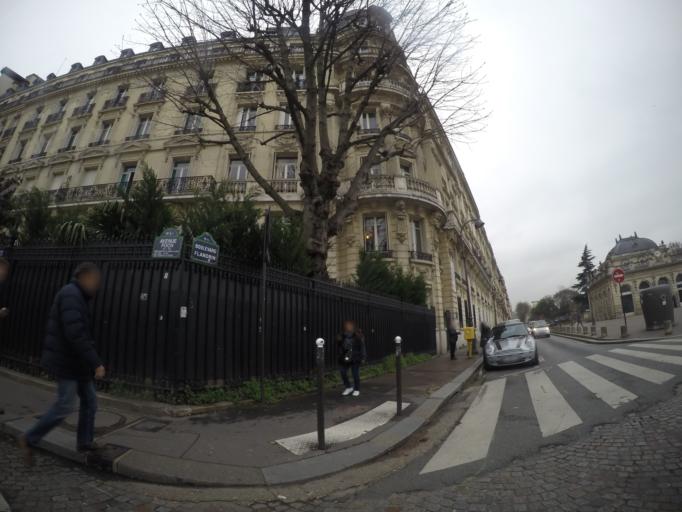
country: FR
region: Ile-de-France
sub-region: Departement des Hauts-de-Seine
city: Neuilly-sur-Seine
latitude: 48.8713
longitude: 2.2762
